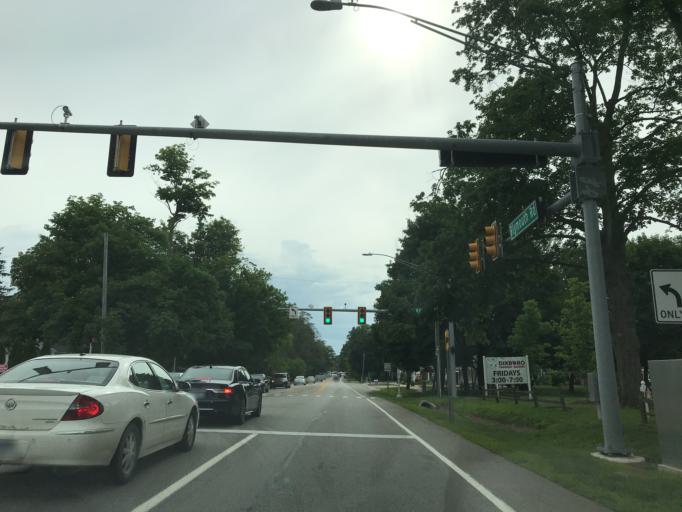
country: US
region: Michigan
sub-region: Washtenaw County
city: Ypsilanti
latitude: 42.3122
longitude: -83.6560
